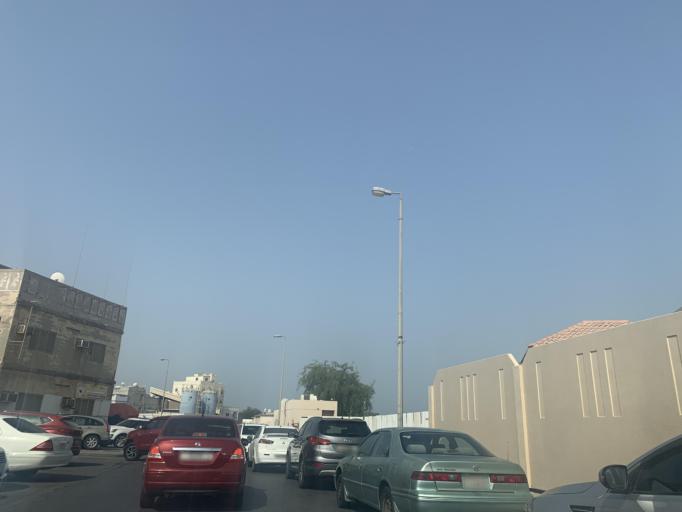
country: BH
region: Manama
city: Jidd Hafs
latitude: 26.2137
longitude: 50.4590
